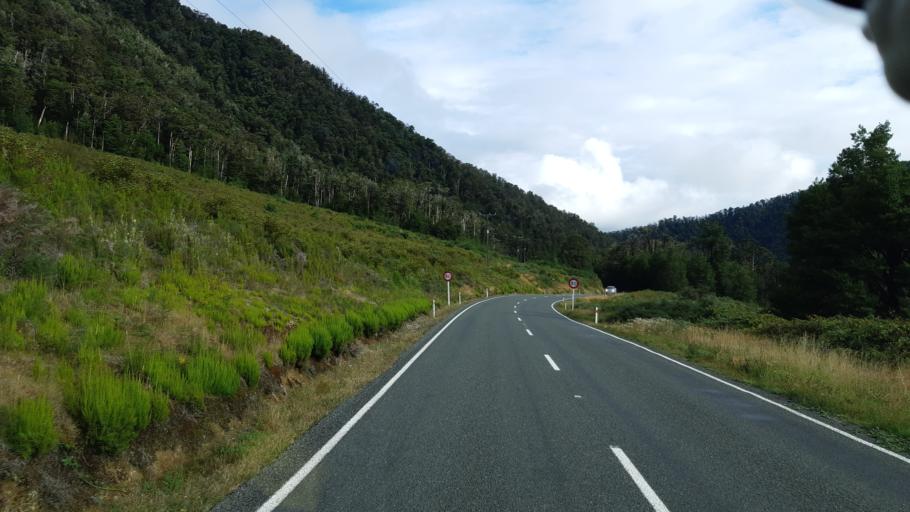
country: NZ
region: West Coast
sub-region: Buller District
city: Westport
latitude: -42.0004
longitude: 172.2270
